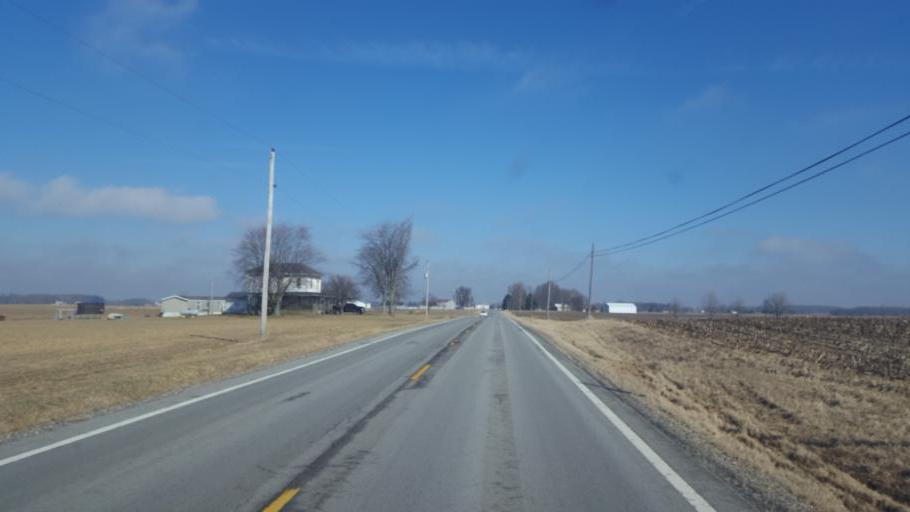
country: US
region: Ohio
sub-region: Crawford County
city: Bucyrus
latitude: 40.9373
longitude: -82.9480
